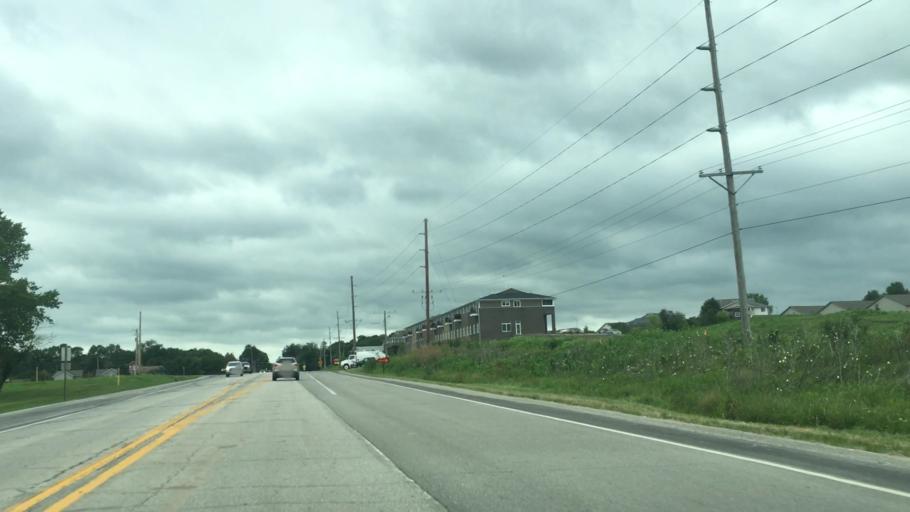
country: US
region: Iowa
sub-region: Johnson County
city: Tiffin
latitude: 41.7066
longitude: -91.6556
